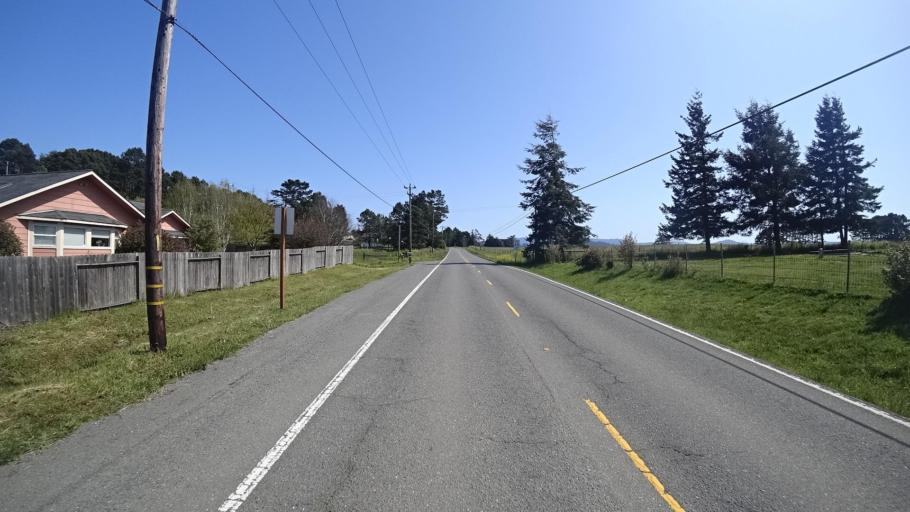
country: US
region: California
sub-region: Humboldt County
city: Hydesville
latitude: 40.5560
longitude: -124.1221
